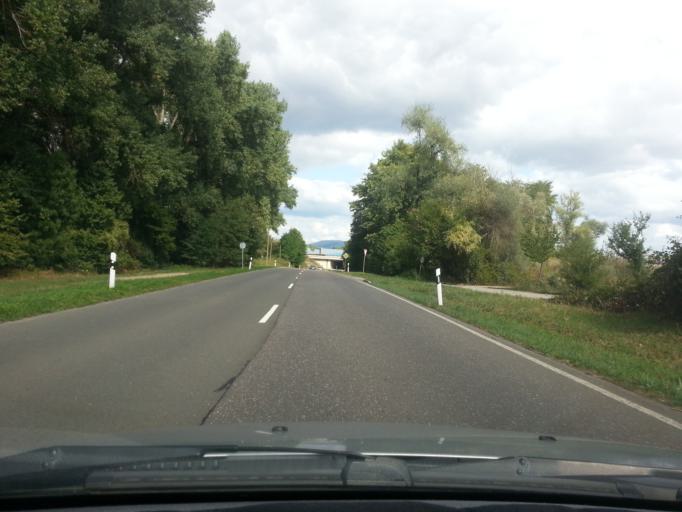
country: DE
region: Baden-Wuerttemberg
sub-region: Karlsruhe Region
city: Malsch
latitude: 49.2696
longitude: 8.6703
